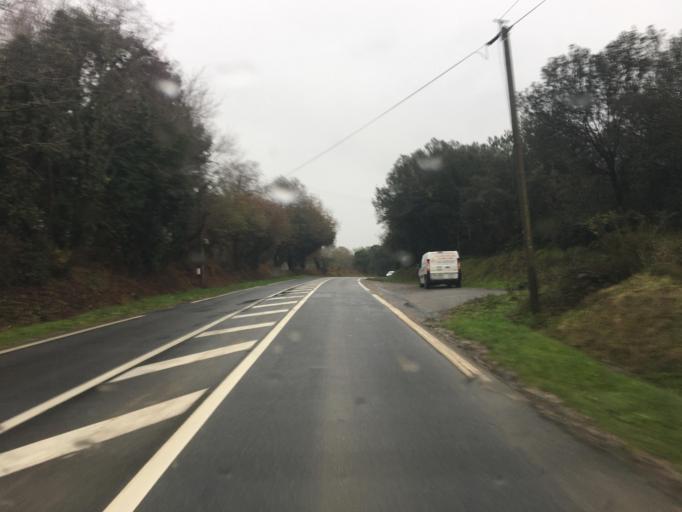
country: FR
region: Pays de la Loire
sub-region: Departement de la Loire-Atlantique
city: La Turballe
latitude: 47.3432
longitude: -2.4794
